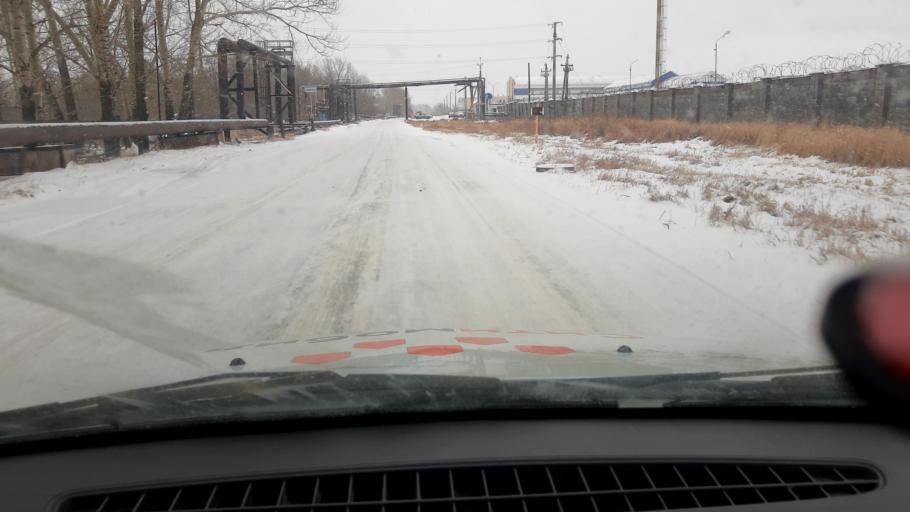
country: RU
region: Bashkortostan
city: Blagoveshchensk
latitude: 54.9141
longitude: 56.0772
